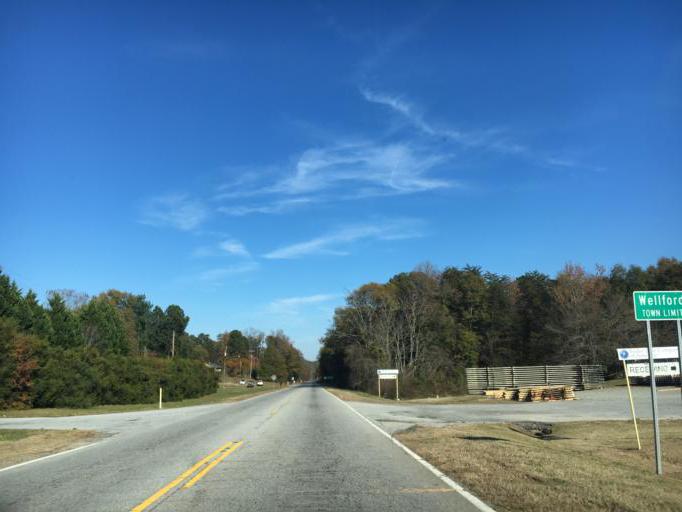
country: US
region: South Carolina
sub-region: Spartanburg County
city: Lyman
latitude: 34.9605
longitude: -82.1203
